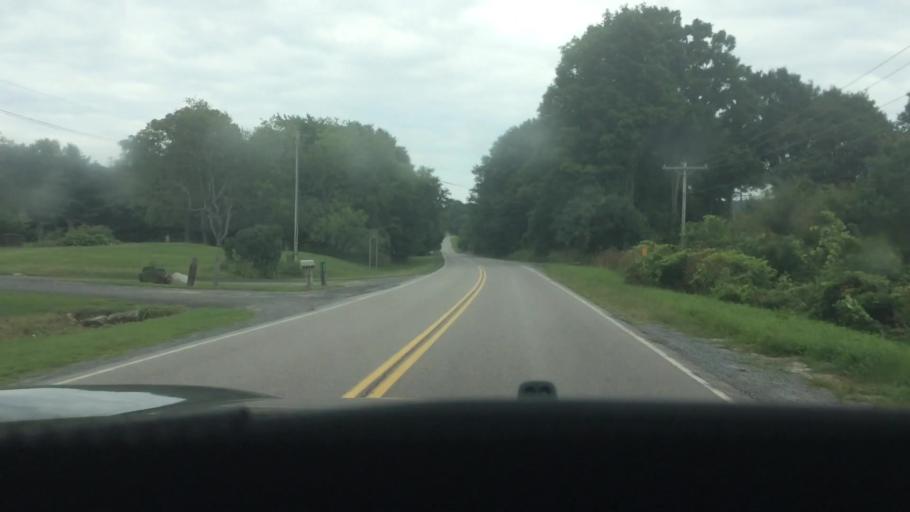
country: US
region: New York
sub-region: St. Lawrence County
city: Canton
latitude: 44.5390
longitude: -75.0763
